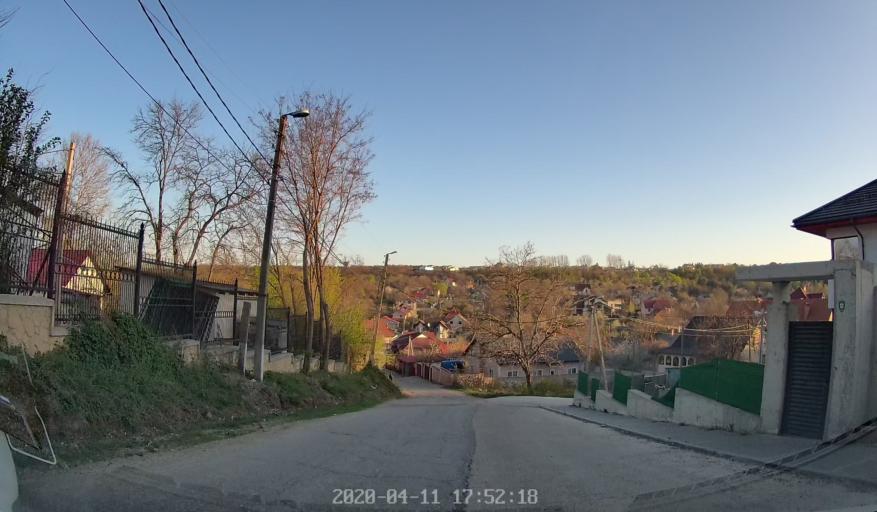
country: MD
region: Chisinau
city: Chisinau
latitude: 46.9732
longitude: 28.8640
